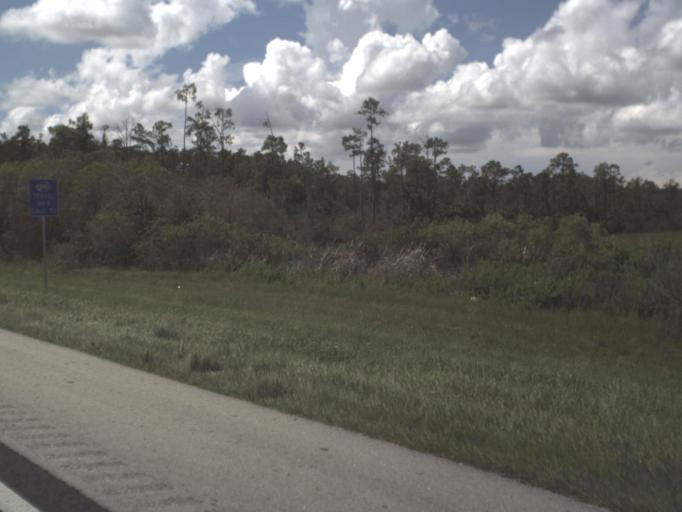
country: US
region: Florida
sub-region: Lee County
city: Fort Myers
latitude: 26.6048
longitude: -81.8011
